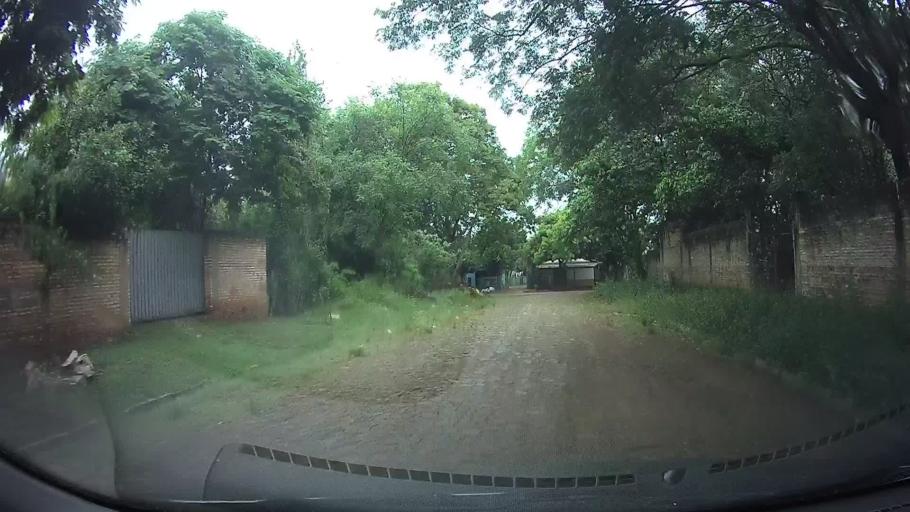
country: PY
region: Central
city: San Lorenzo
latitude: -25.2664
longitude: -57.4778
